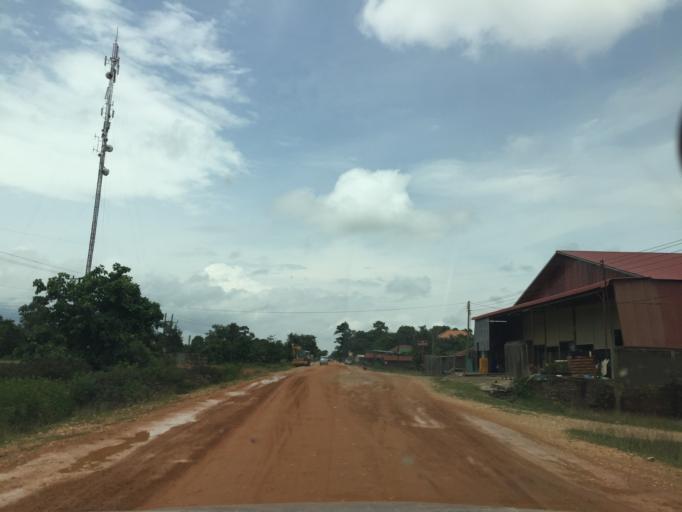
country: LA
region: Attapu
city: Attapu
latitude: 14.6842
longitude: 106.5919
